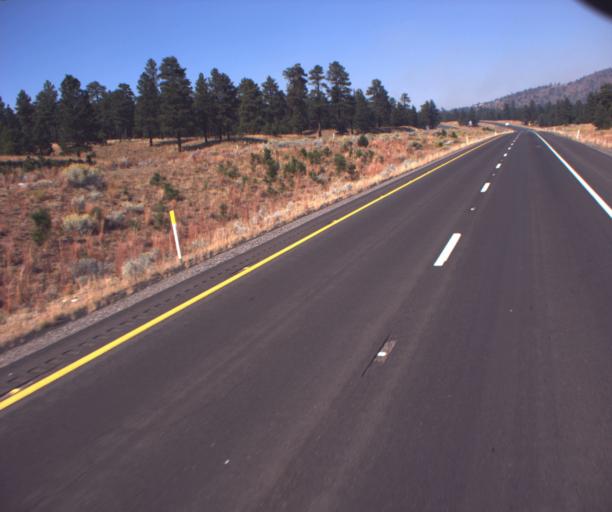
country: US
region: Arizona
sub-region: Coconino County
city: Flagstaff
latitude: 35.3610
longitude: -111.5707
